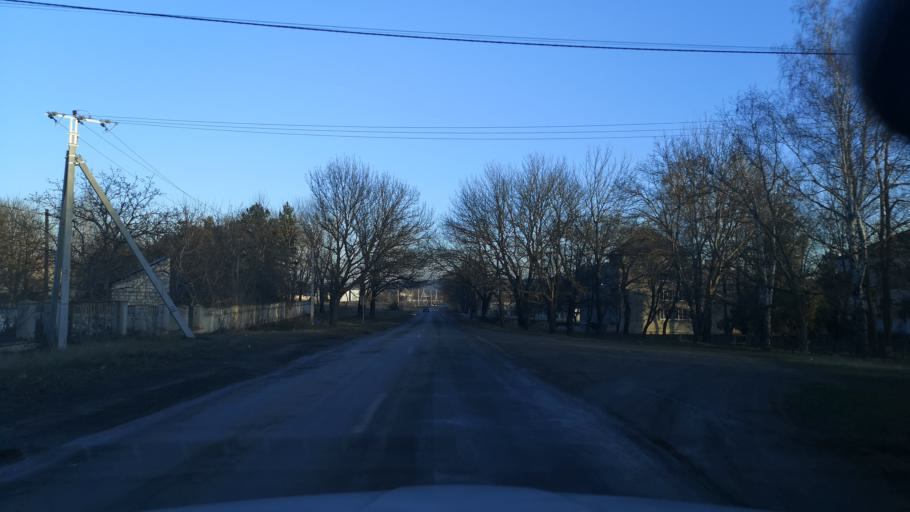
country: MD
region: Orhei
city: Orhei
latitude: 47.2878
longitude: 28.8606
